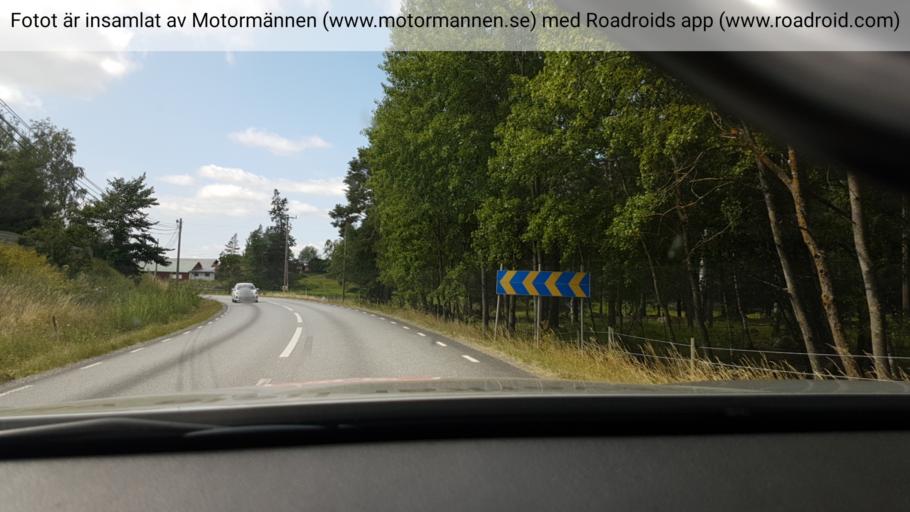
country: SE
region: Stockholm
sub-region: Vallentuna Kommun
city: Vallentuna
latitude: 59.5436
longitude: 18.1748
